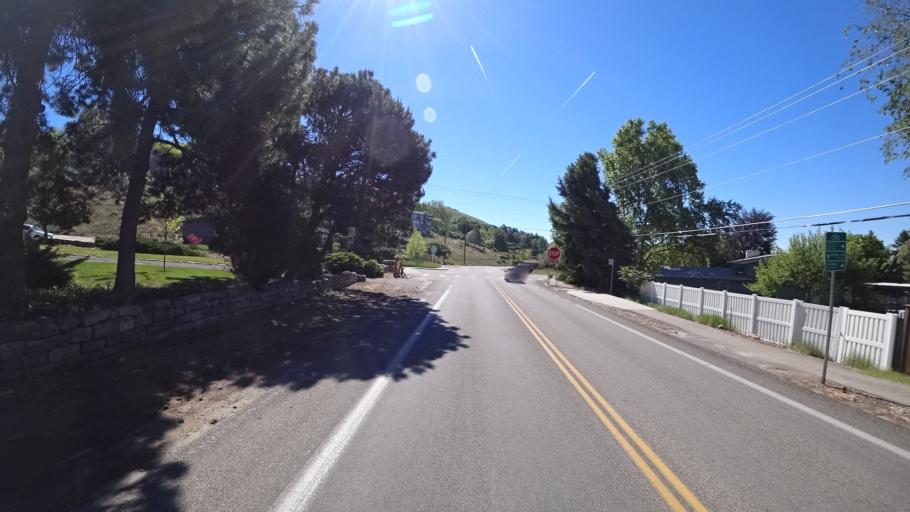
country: US
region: Idaho
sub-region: Ada County
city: Garden City
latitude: 43.6662
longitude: -116.2489
